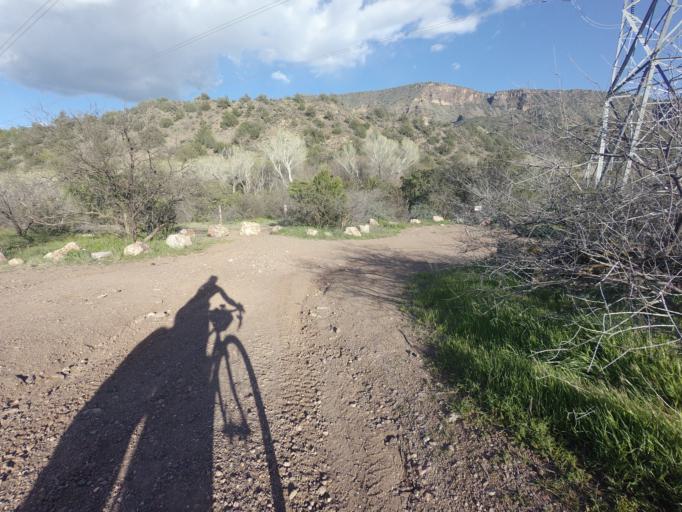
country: US
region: Arizona
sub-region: Gila County
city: Pine
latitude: 34.3842
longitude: -111.6589
